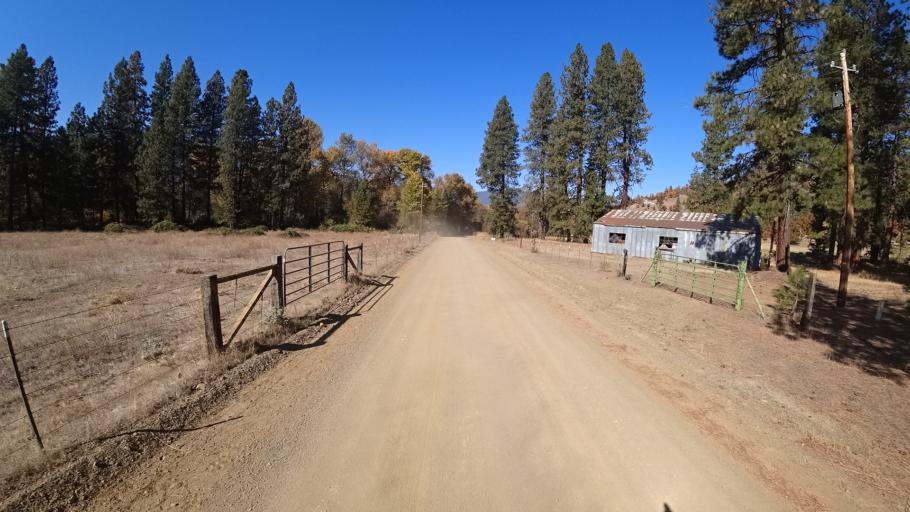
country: US
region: California
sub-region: Siskiyou County
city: Yreka
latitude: 41.6027
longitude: -122.9585
